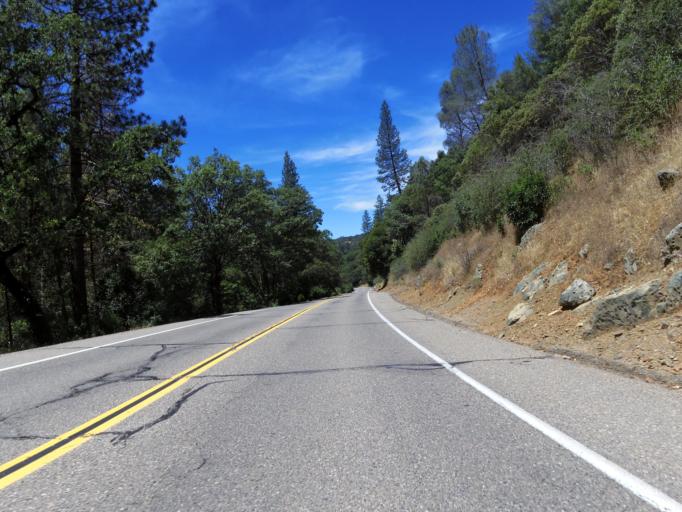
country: US
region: California
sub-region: Mariposa County
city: Midpines
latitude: 37.5194
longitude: -119.9457
